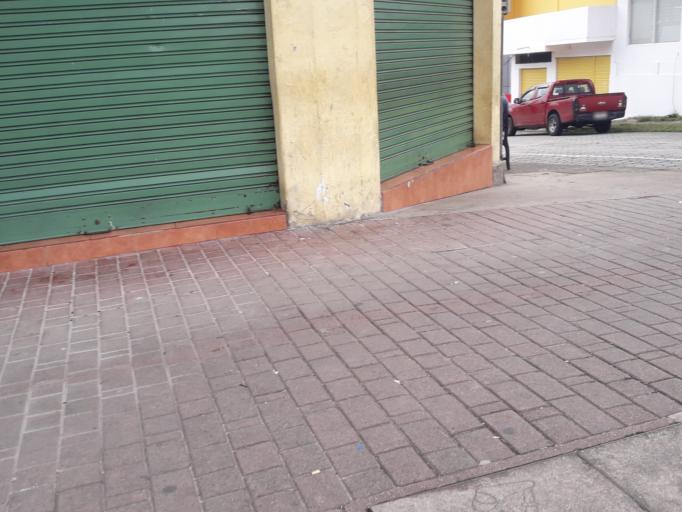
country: EC
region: Napo
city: Tena
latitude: -1.0006
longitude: -77.8116
